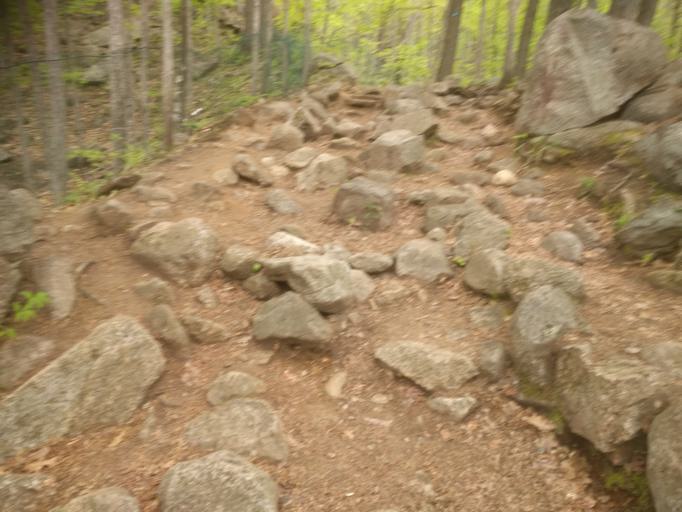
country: CA
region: Quebec
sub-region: Outaouais
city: Wakefield
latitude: 45.5347
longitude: -75.9929
